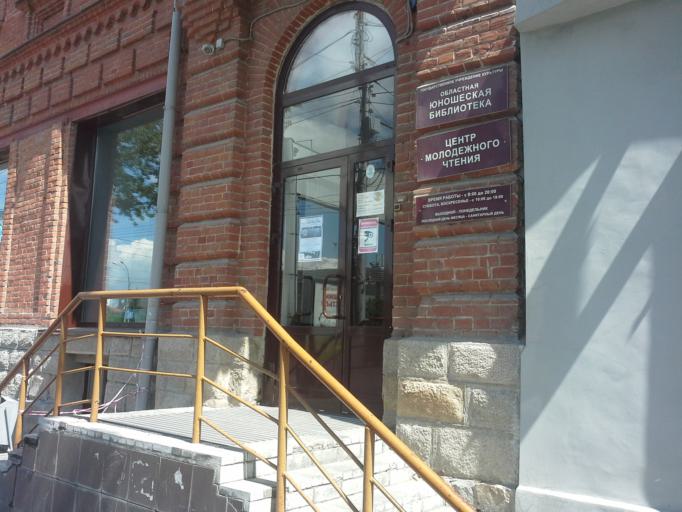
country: RU
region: Novosibirsk
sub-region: Novosibirskiy Rayon
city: Novosibirsk
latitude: 55.0243
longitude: 82.9223
